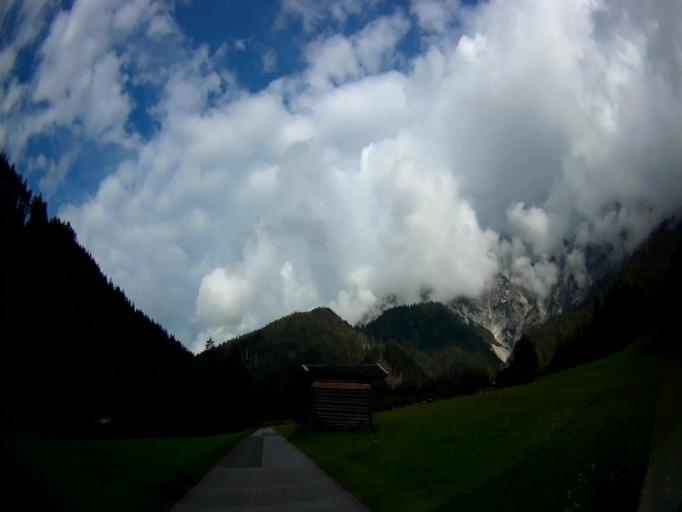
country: AT
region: Salzburg
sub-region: Politischer Bezirk Zell am See
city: Leogang
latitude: 47.4497
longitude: 12.7637
